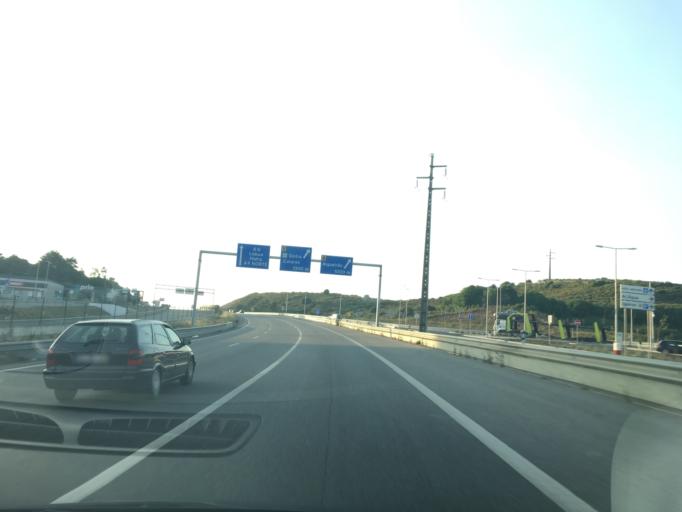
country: PT
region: Lisbon
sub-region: Sintra
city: Sintra
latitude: 38.7917
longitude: -9.3579
